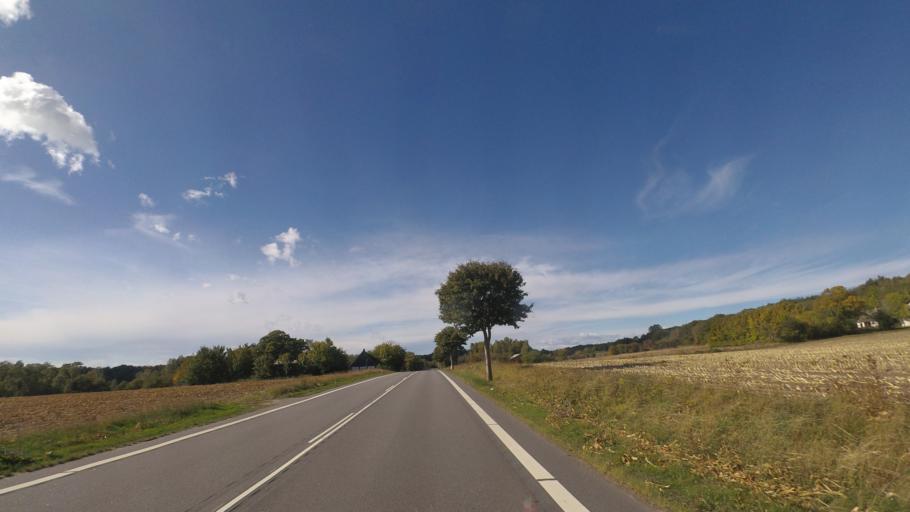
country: DK
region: Capital Region
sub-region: Bornholm Kommune
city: Ronne
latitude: 55.0784
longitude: 14.7654
